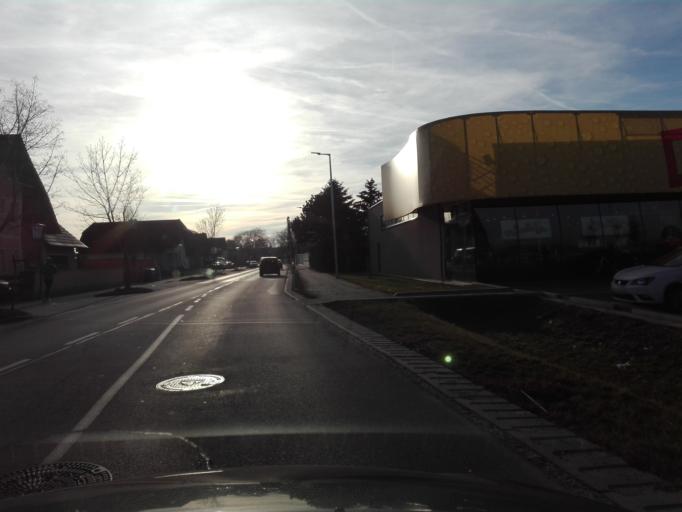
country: AT
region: Lower Austria
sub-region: Politischer Bezirk Amstetten
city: Sankt Valentin
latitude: 48.1611
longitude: 14.5149
